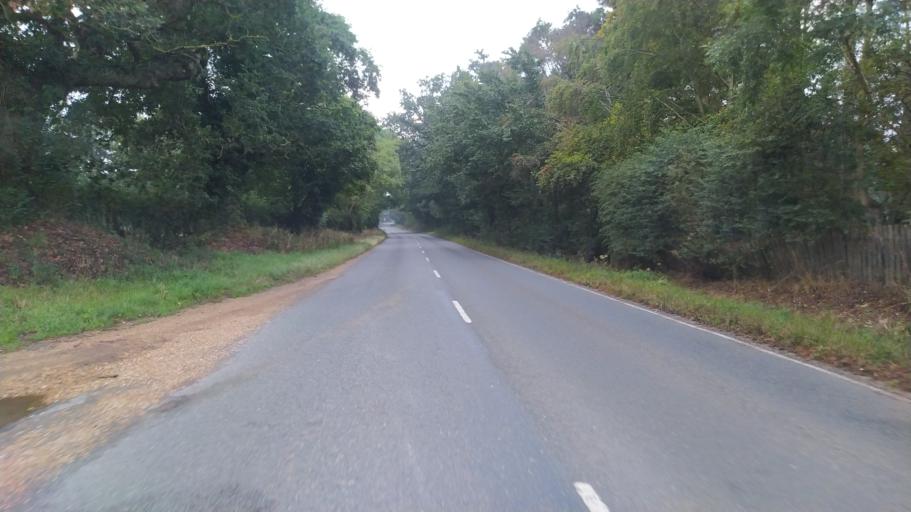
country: GB
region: England
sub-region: Hampshire
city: New Milton
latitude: 50.7675
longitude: -1.6975
